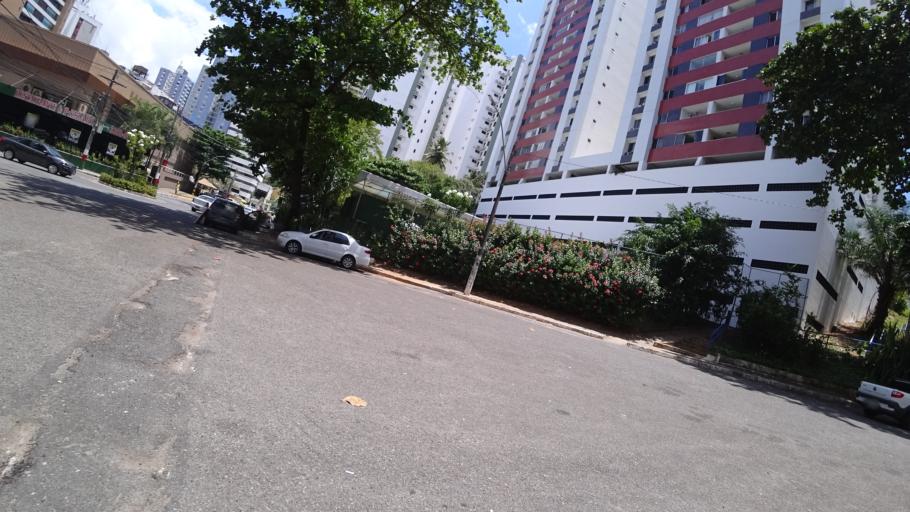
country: BR
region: Bahia
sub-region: Salvador
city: Salvador
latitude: -13.0041
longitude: -38.4635
